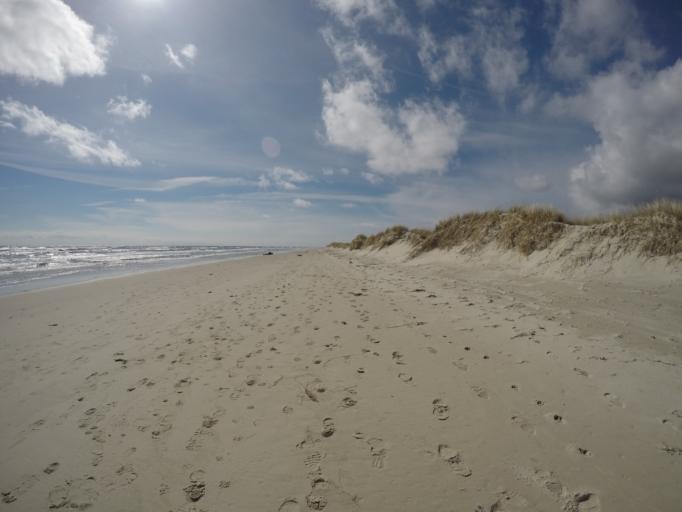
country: SE
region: Skane
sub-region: Simrishamns Kommun
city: Simrishamn
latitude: 55.3963
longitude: 14.2117
